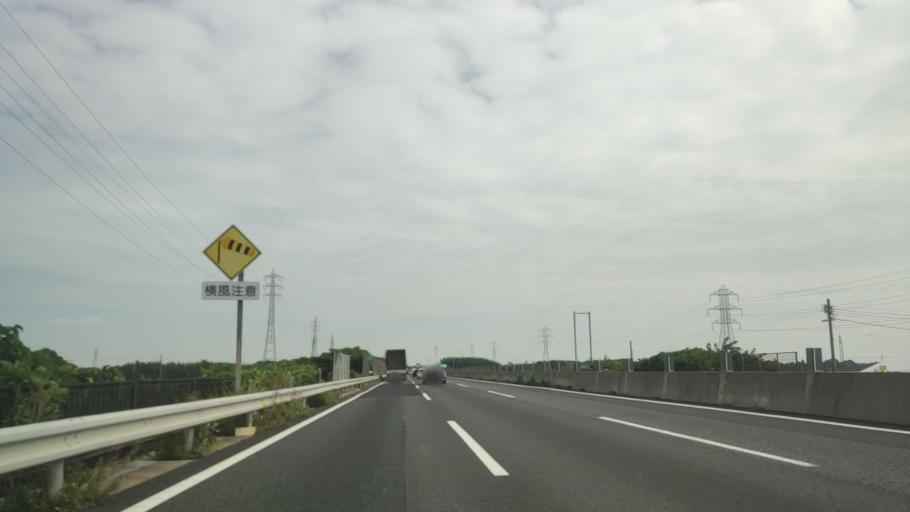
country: JP
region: Mie
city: Komono
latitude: 34.9992
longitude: 136.5592
